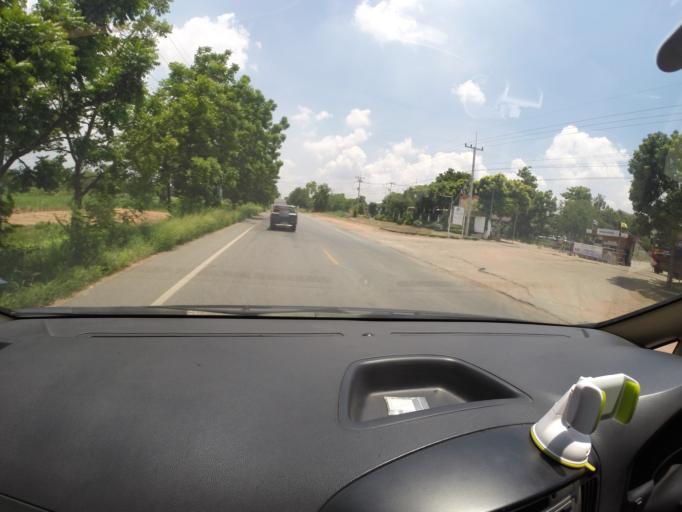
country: TH
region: Nakhon Ratchasima
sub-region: Amphoe Thepharak
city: Thepharak
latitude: 15.1276
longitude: 101.5557
